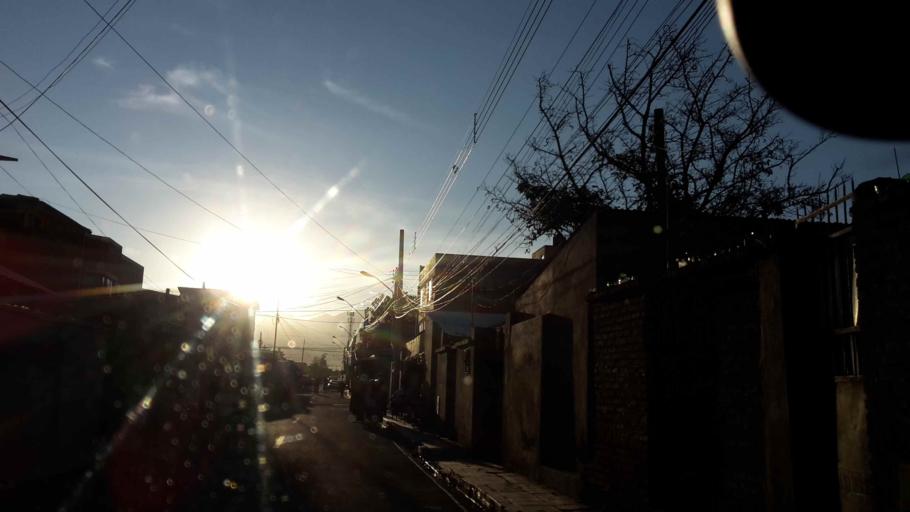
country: BO
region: Cochabamba
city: Cochabamba
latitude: -17.3620
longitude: -66.1826
